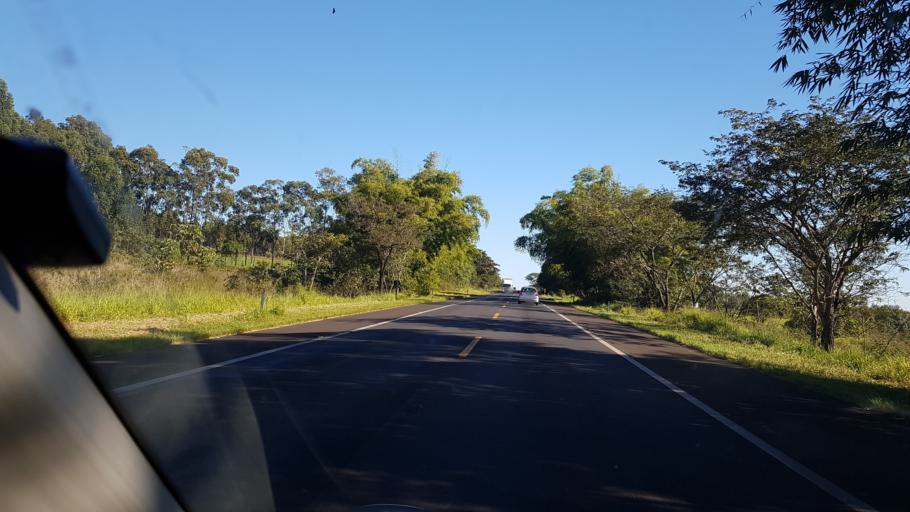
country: BR
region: Sao Paulo
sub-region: Assis
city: Assis
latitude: -22.6259
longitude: -50.4468
